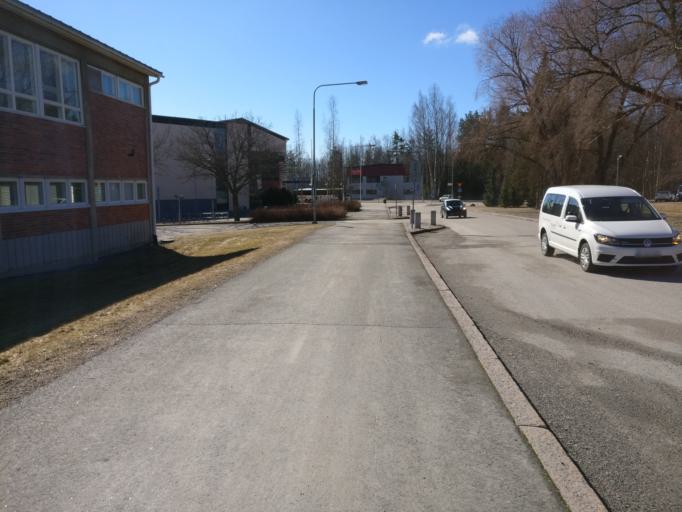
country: FI
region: Uusimaa
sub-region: Helsinki
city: Jaervenpaeae
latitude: 60.4816
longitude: 25.0811
